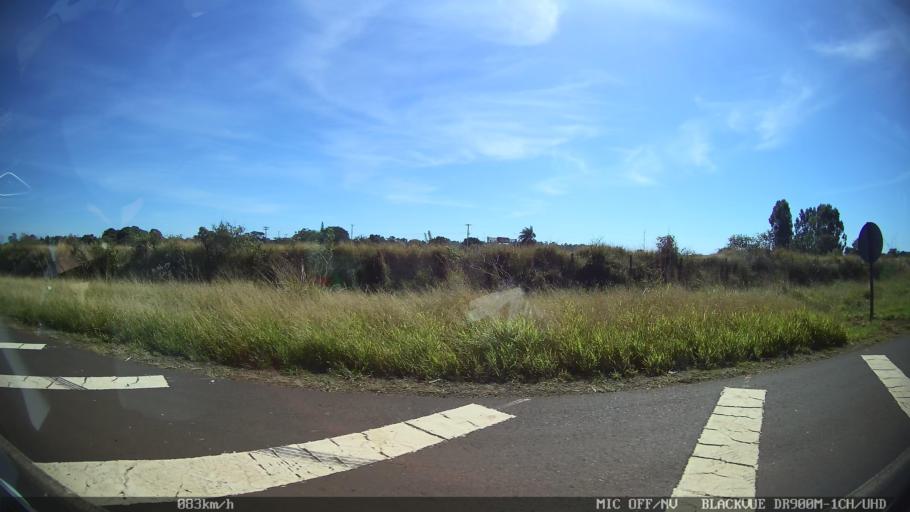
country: BR
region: Sao Paulo
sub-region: Franca
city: Franca
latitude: -20.5475
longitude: -47.4796
